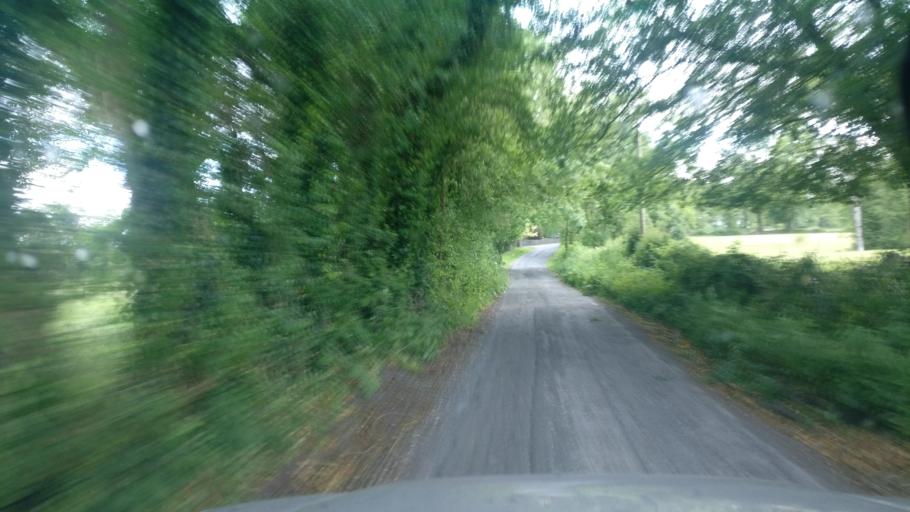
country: IE
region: Connaught
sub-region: County Galway
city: Ballinasloe
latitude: 53.2329
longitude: -8.2105
